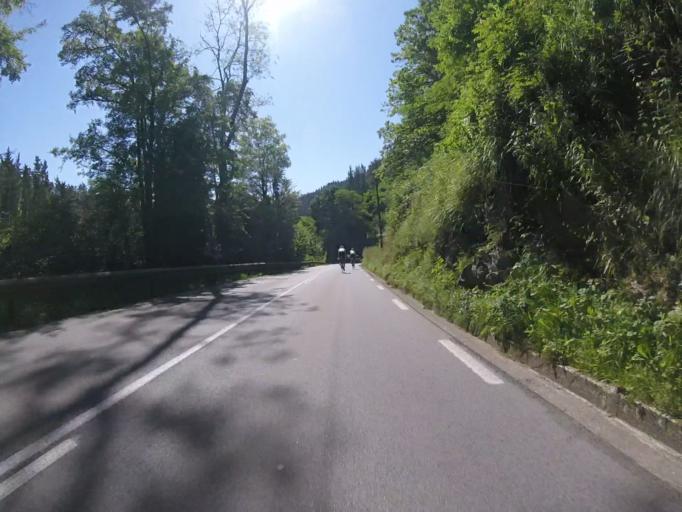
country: ES
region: Basque Country
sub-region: Provincia de Guipuzcoa
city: Alegria de Oria
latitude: 43.1239
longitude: -2.1094
